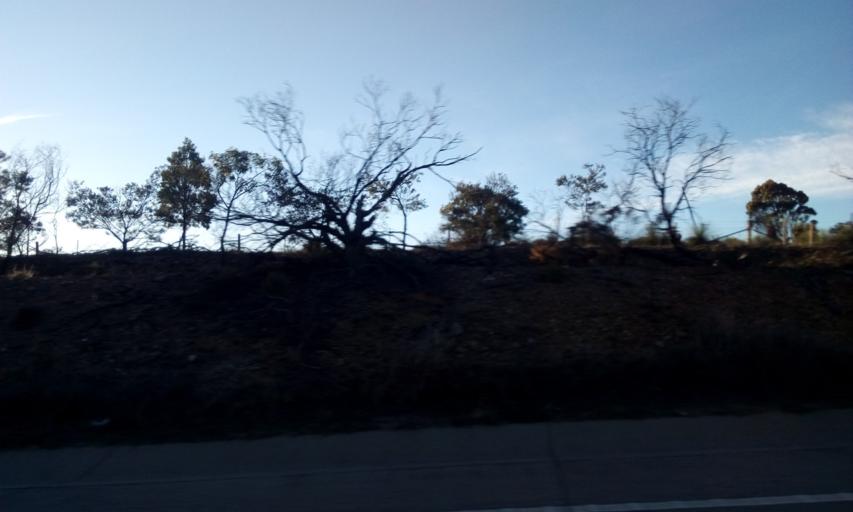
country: AU
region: New South Wales
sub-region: Yass Valley
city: Gundaroo
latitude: -35.1037
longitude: 149.3733
